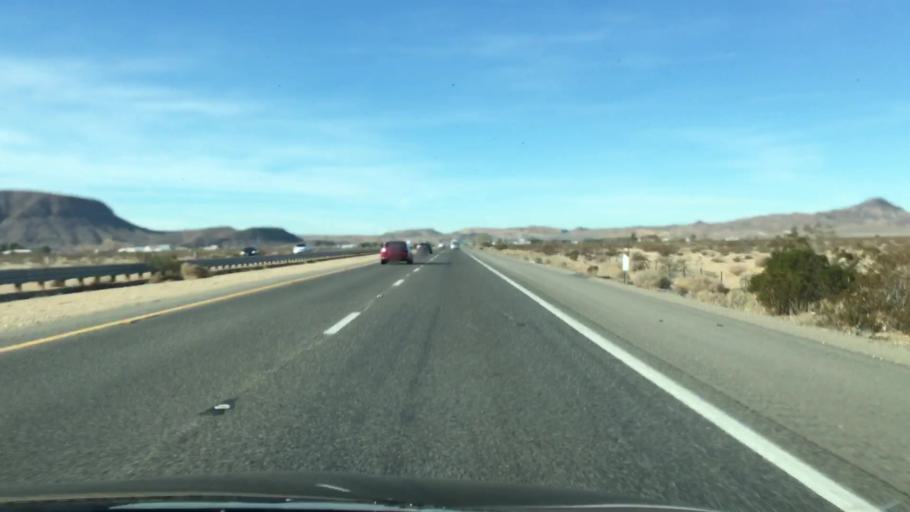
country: US
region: California
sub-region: San Bernardino County
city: Barstow
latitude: 34.9057
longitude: -116.8656
